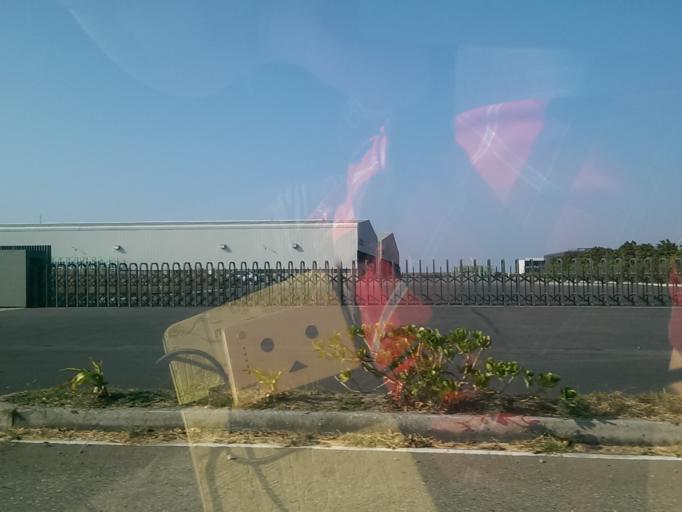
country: TW
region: Taiwan
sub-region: Changhua
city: Chang-hua
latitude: 24.0771
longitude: 120.3881
